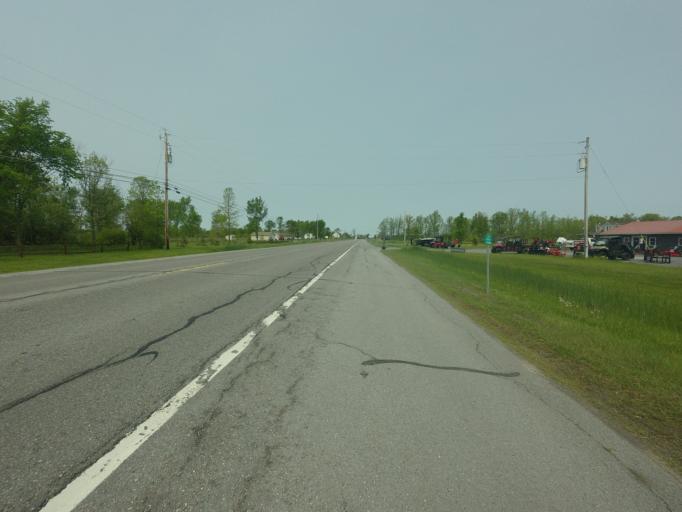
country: US
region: New York
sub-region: Jefferson County
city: Dexter
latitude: 44.0400
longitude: -76.0759
